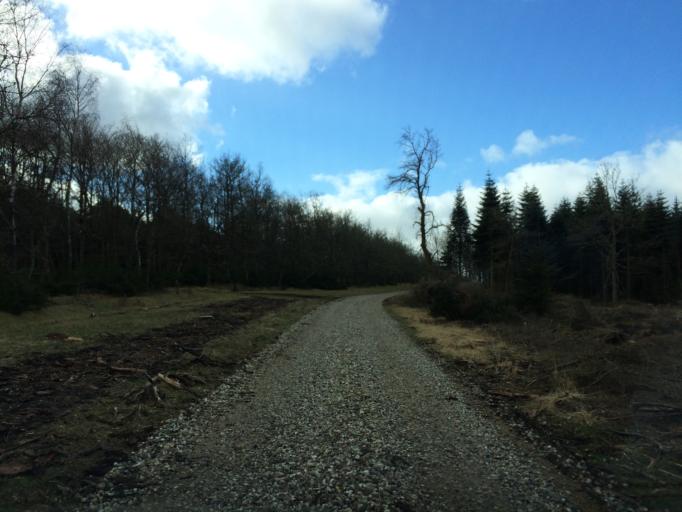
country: DK
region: Central Jutland
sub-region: Holstebro Kommune
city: Ulfborg
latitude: 56.2702
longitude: 8.4512
